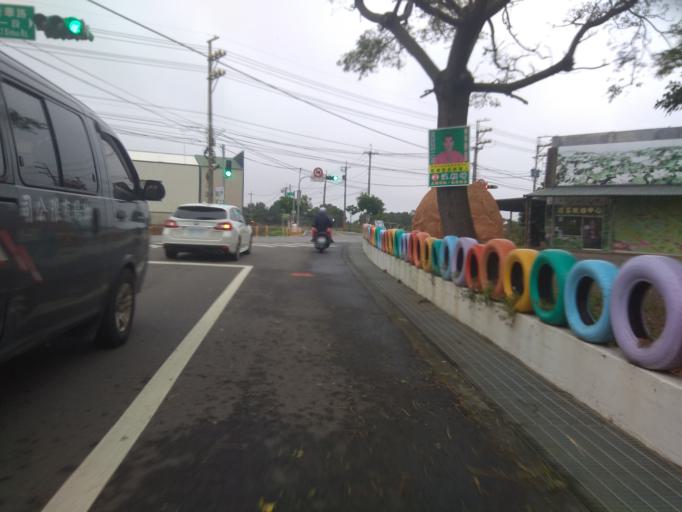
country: TW
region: Taiwan
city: Taoyuan City
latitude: 24.9992
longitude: 121.1220
